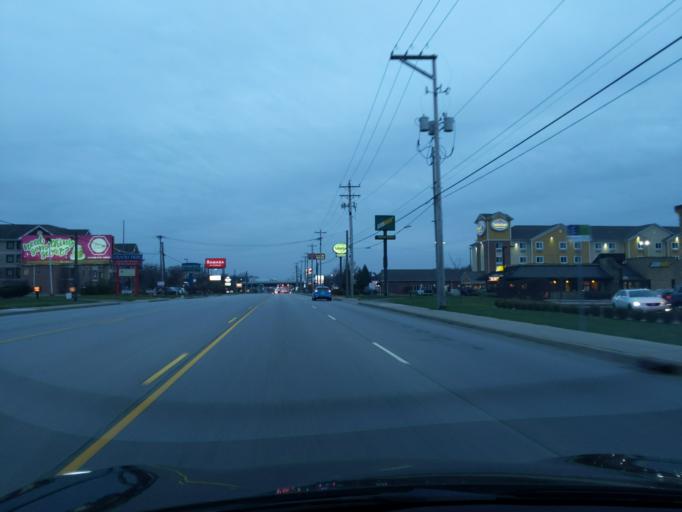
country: US
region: Indiana
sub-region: Saint Joseph County
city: Georgetown
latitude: 41.7255
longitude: -86.2505
